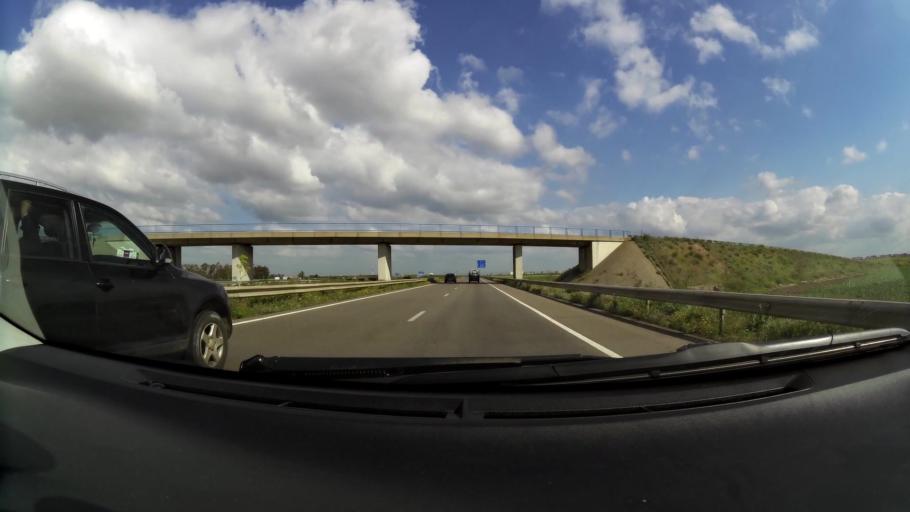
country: MA
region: Chaouia-Ouardigha
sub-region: Settat Province
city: Berrechid
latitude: 33.3067
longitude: -7.5853
